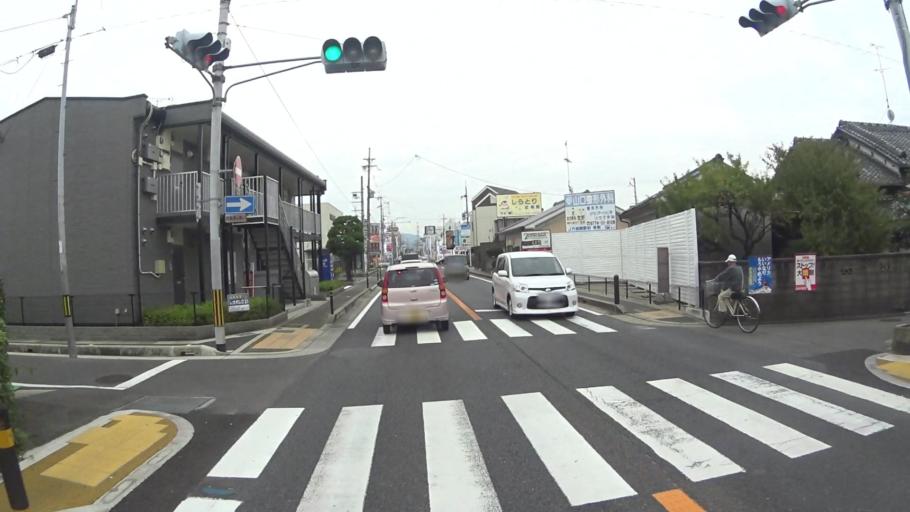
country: JP
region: Kyoto
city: Tanabe
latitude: 34.8555
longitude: 135.7782
